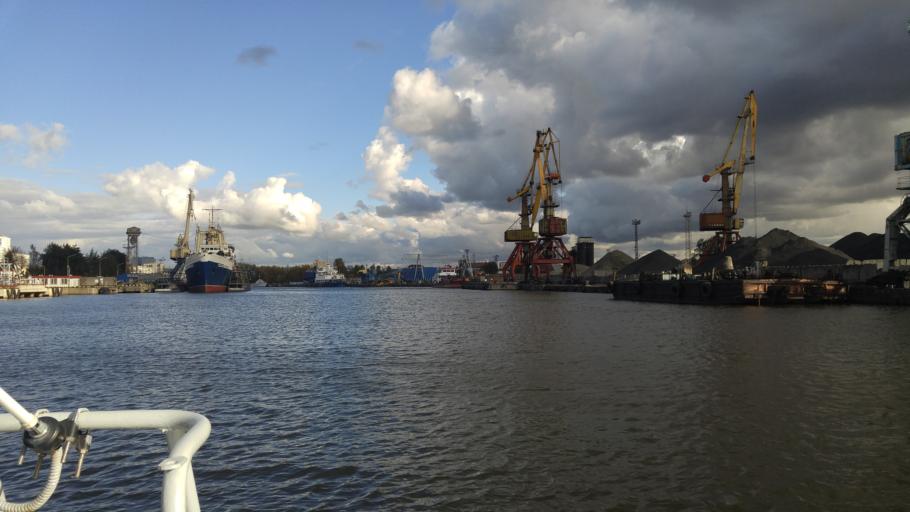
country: RU
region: Kaliningrad
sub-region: Gorod Kaliningrad
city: Kaliningrad
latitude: 54.7040
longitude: 20.4798
